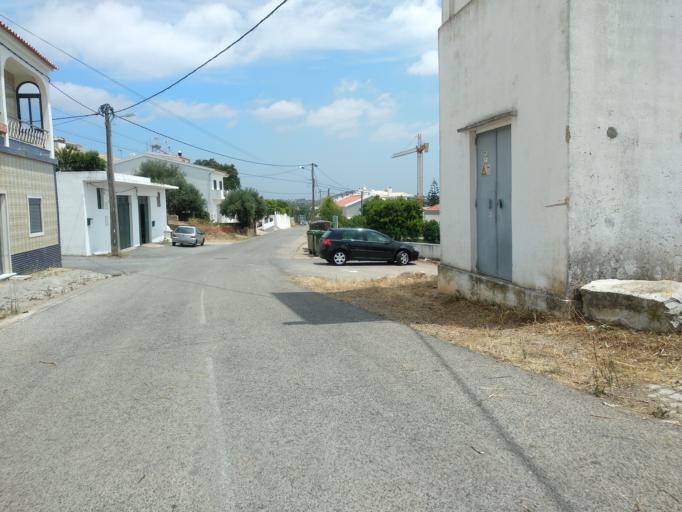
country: PT
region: Faro
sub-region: Sao Bras de Alportel
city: Sao Bras de Alportel
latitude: 37.1626
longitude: -7.8882
